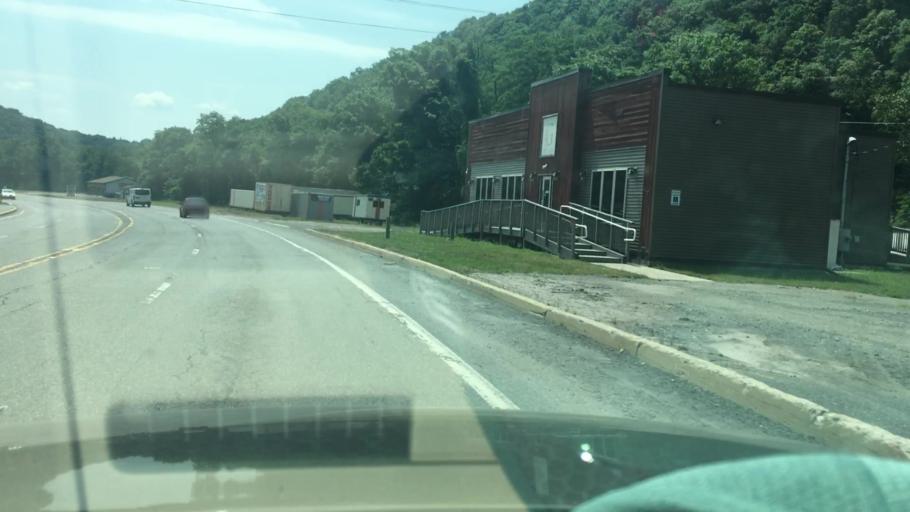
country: US
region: Pennsylvania
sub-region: Schuylkill County
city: Tamaqua
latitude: 40.7768
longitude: -75.9609
